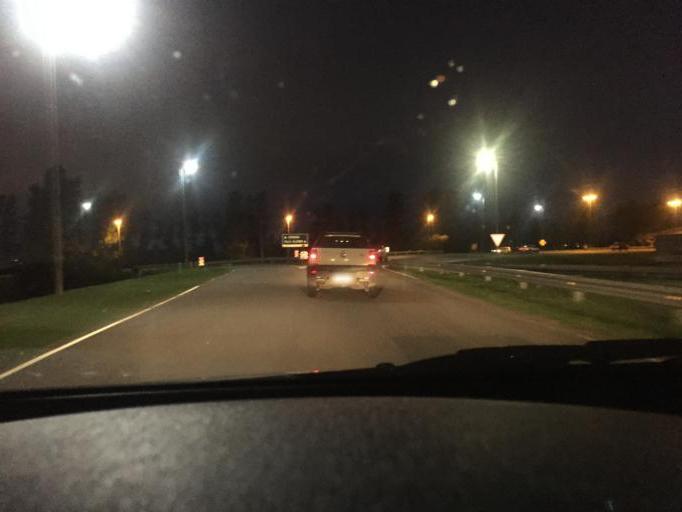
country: AR
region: Cordoba
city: Villa Allende
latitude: -31.3032
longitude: -64.2242
